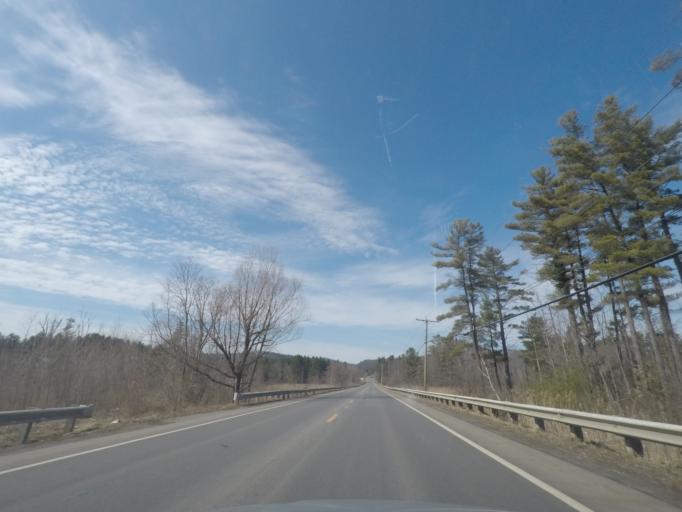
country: US
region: Massachusetts
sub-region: Berkshire County
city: Stockbridge
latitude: 42.2962
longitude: -73.3281
